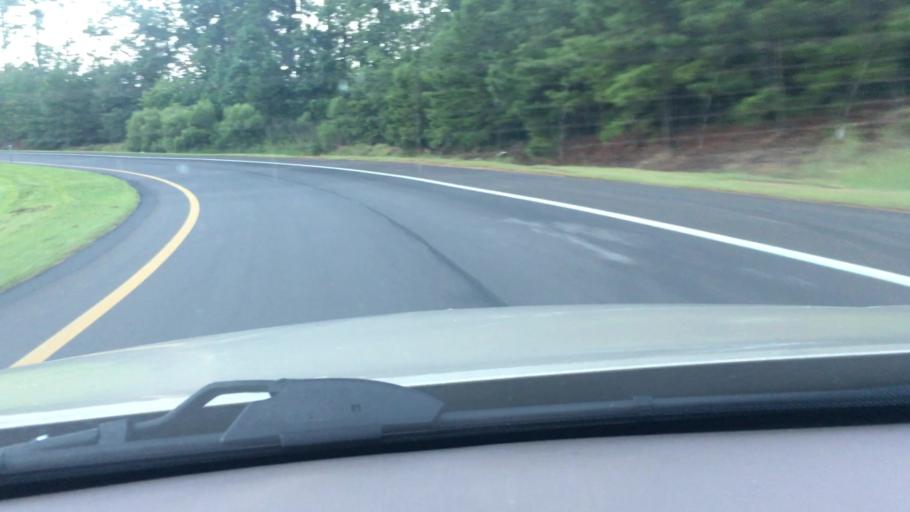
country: US
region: South Carolina
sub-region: Lexington County
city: Irmo
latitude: 34.1005
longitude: -81.1733
